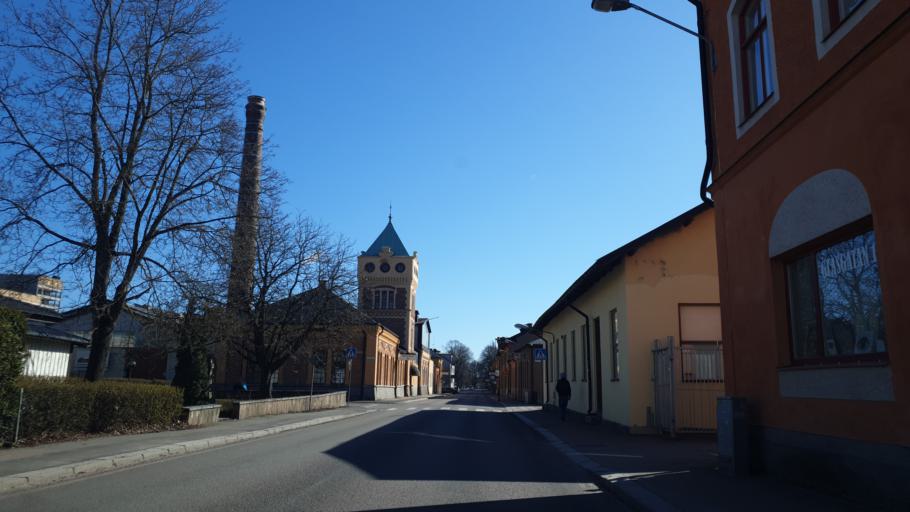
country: SE
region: Vaestmanland
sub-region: Kopings Kommun
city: Koping
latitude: 59.5113
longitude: 15.9996
